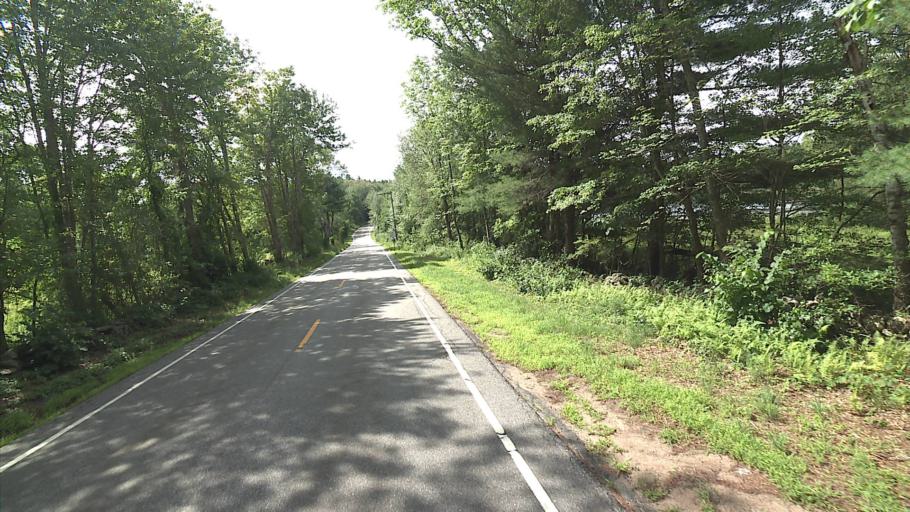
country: US
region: Massachusetts
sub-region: Hampden County
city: Holland
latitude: 41.9731
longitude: -72.1129
